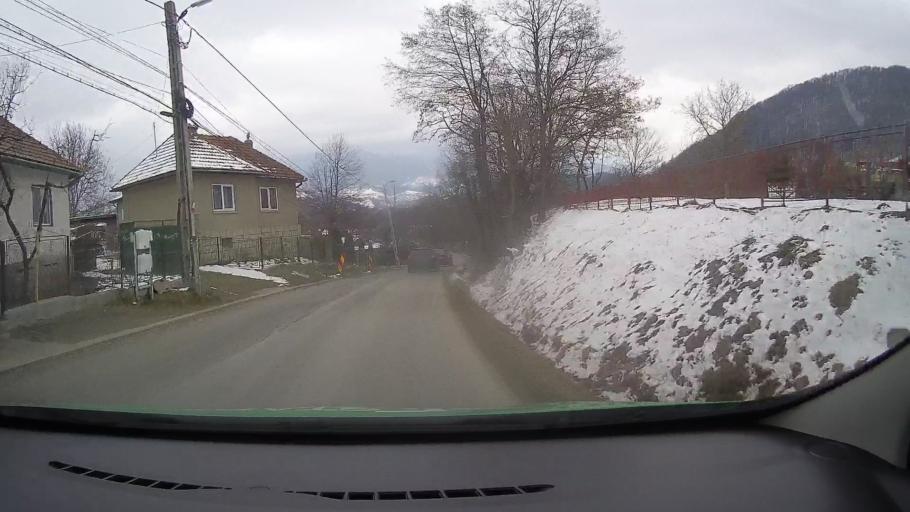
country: RO
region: Brasov
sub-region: Comuna Bran
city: Bran
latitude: 45.5267
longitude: 25.3629
